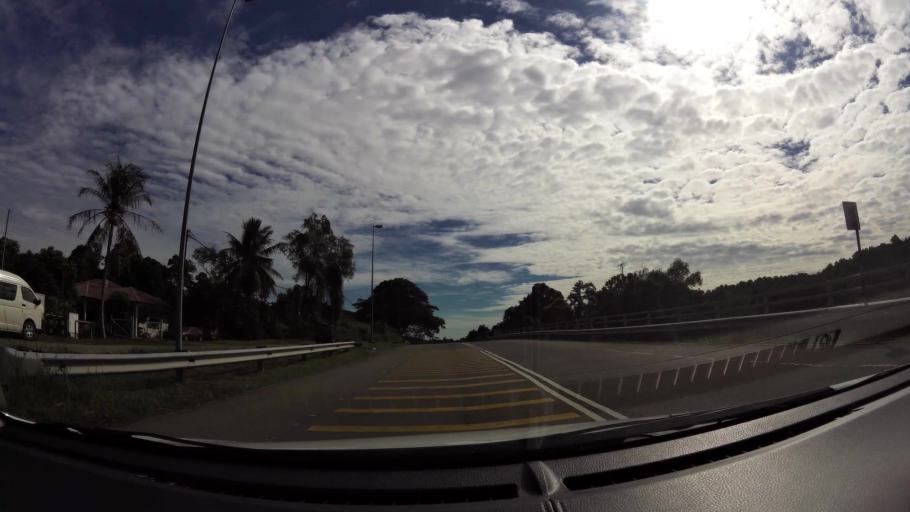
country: BN
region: Brunei and Muara
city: Bandar Seri Begawan
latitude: 4.8991
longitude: 114.9730
